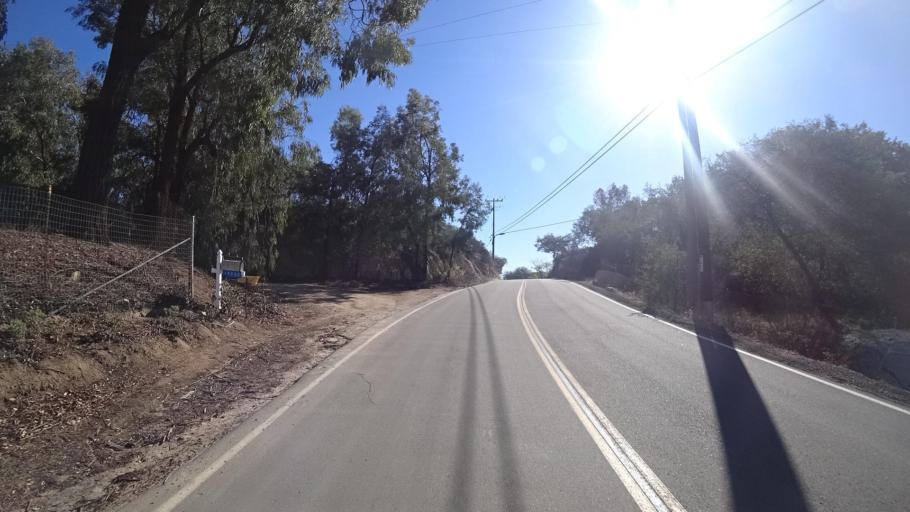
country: MX
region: Baja California
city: Tecate
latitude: 32.6754
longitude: -116.7163
